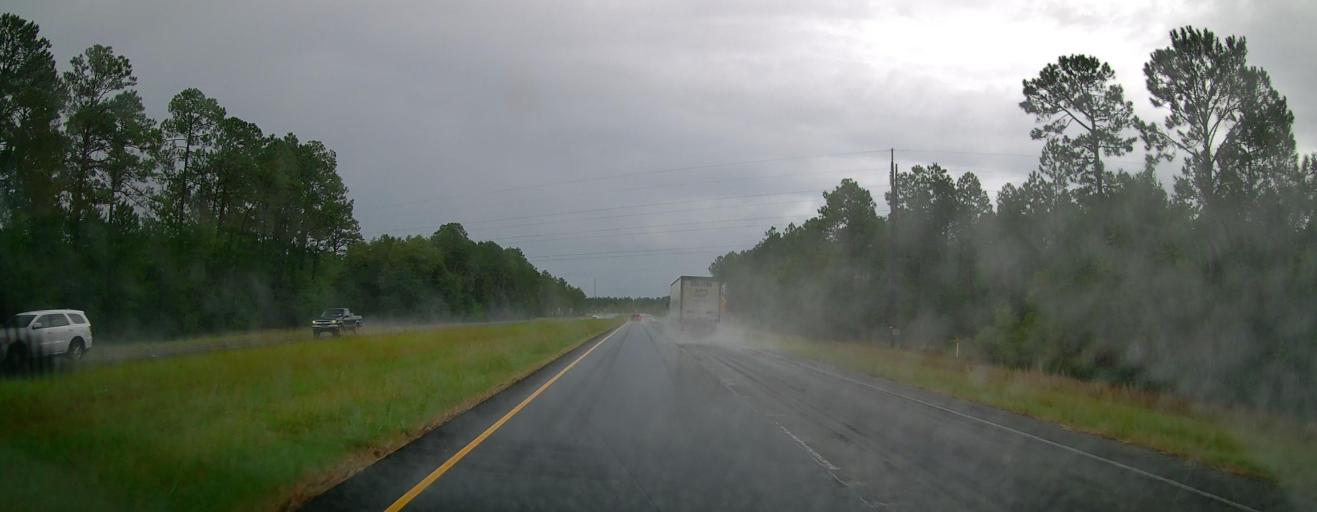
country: US
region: Georgia
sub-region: Ware County
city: Deenwood
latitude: 31.2148
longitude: -82.4198
